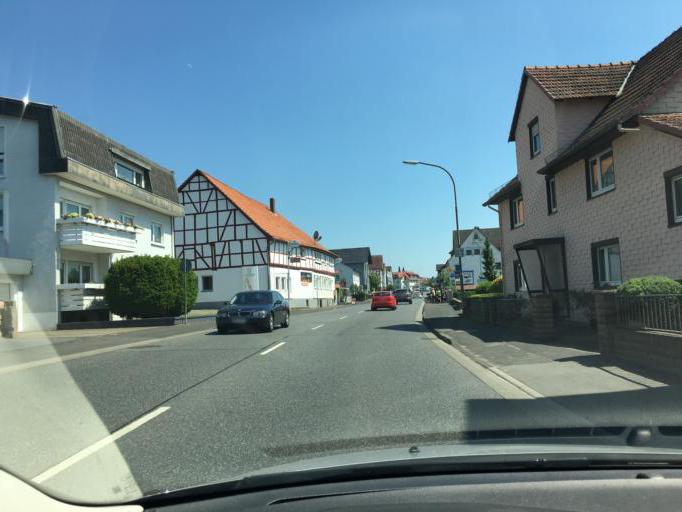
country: DE
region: Hesse
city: Bebra
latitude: 50.9936
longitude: 9.7695
